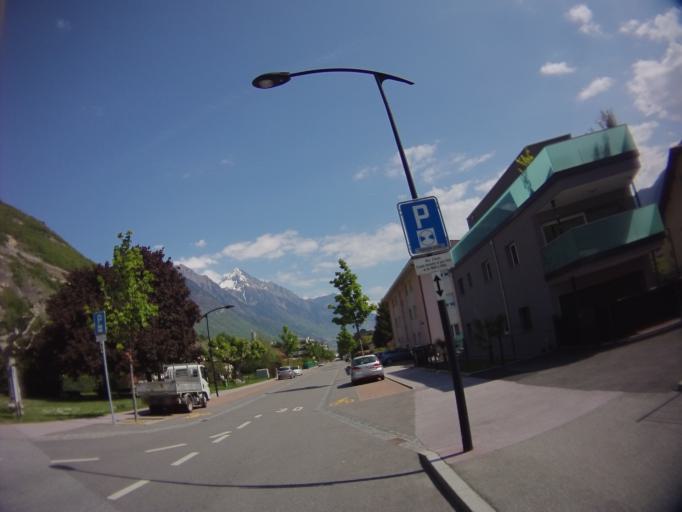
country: CH
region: Valais
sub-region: Martigny District
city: Martigny-Ville
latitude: 46.0955
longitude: 7.0633
